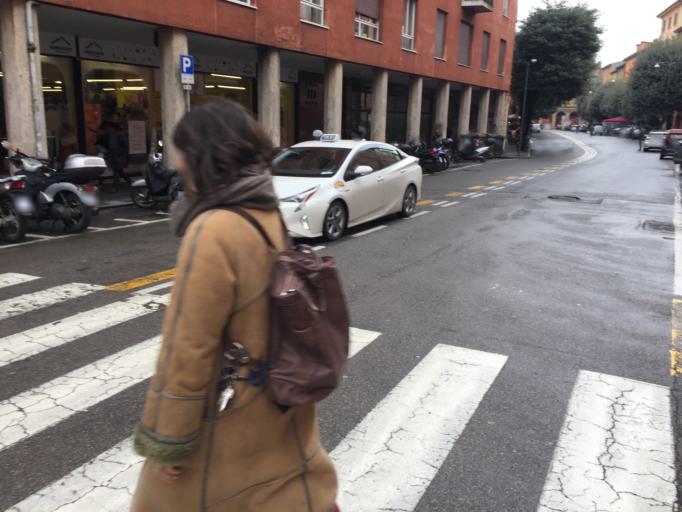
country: IT
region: Emilia-Romagna
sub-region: Provincia di Bologna
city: Bologna
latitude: 44.4987
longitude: 11.3463
